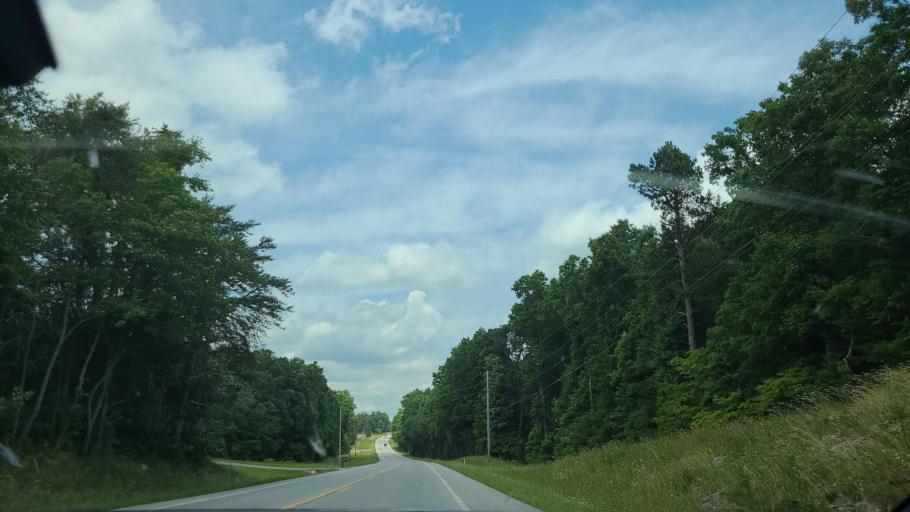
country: US
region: Tennessee
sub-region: Cumberland County
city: Lake Tansi
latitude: 35.8212
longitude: -85.0191
